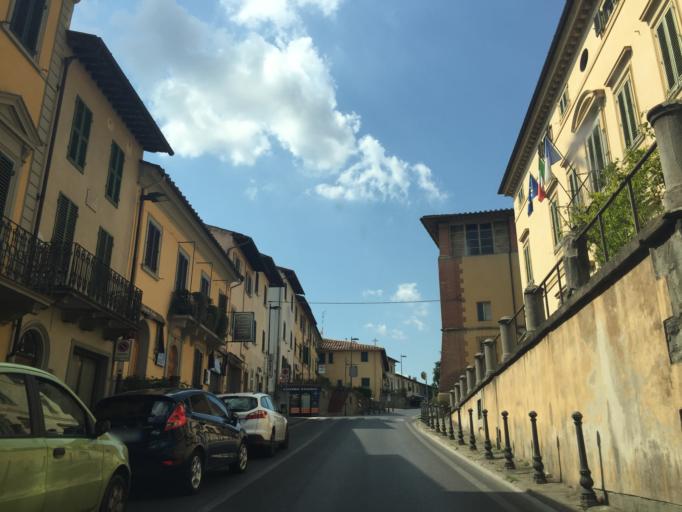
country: IT
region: Tuscany
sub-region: Provincia di Prato
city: Poggio A Caiano
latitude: 43.8161
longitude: 11.0565
